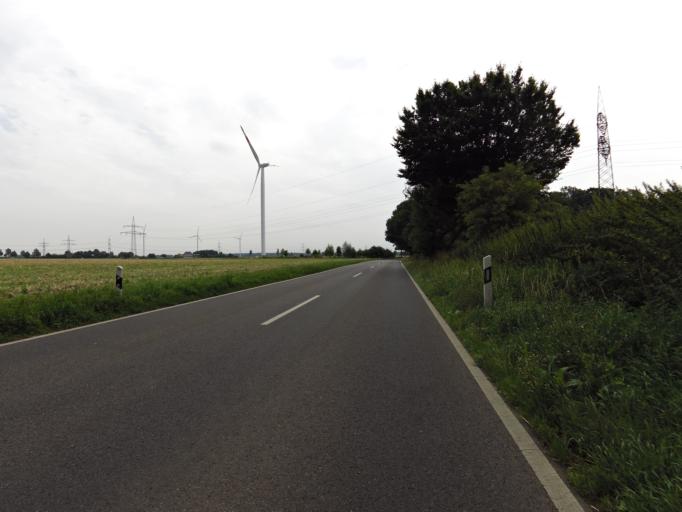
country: DE
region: North Rhine-Westphalia
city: Geilenkirchen
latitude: 51.0056
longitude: 6.1104
